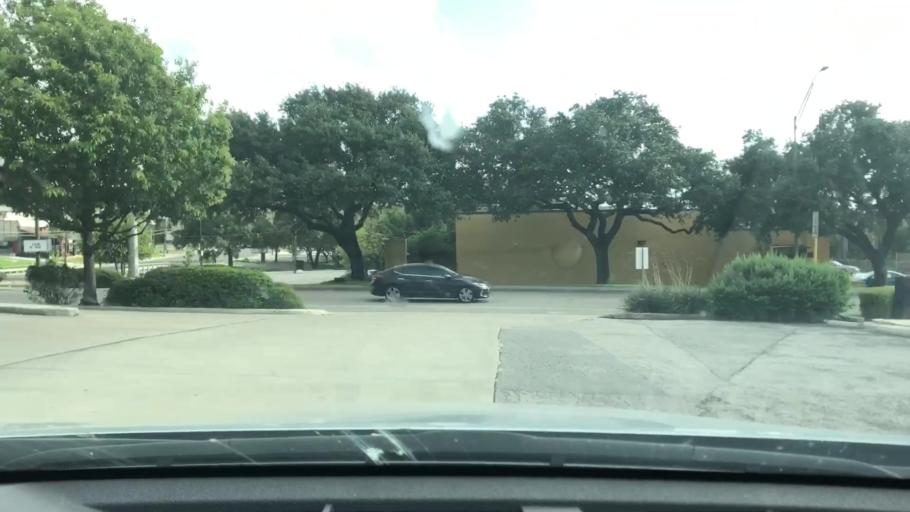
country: US
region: Texas
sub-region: Bexar County
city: Balcones Heights
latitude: 29.5240
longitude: -98.5684
